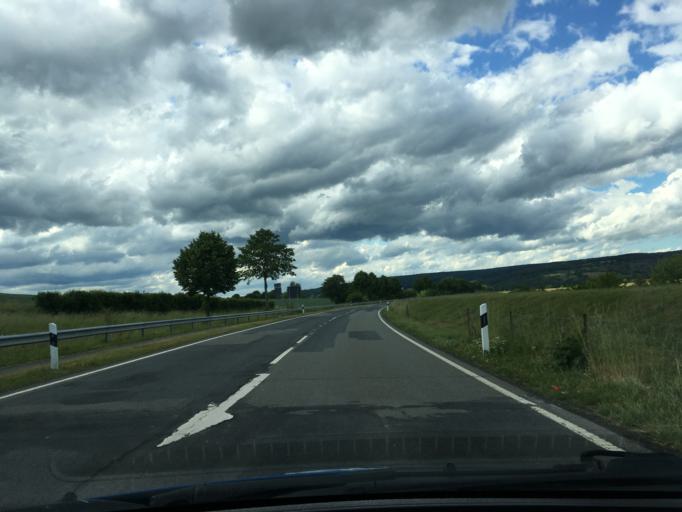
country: DE
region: Lower Saxony
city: Einbeck
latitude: 51.7858
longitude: 9.8985
